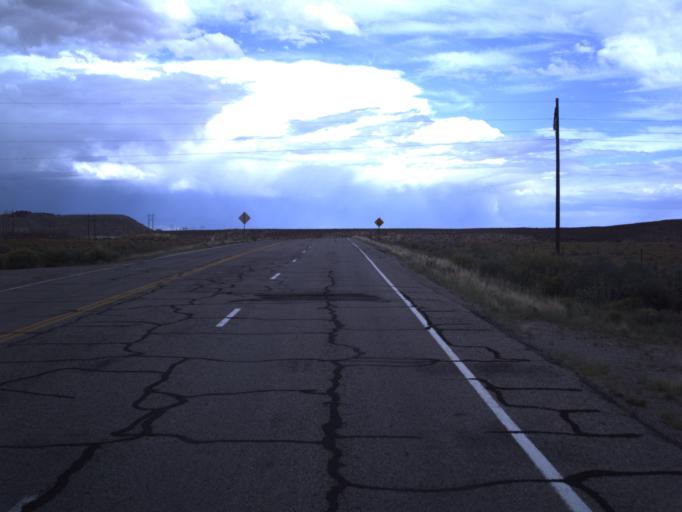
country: US
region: Utah
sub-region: San Juan County
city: Blanding
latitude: 37.2802
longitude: -109.3748
